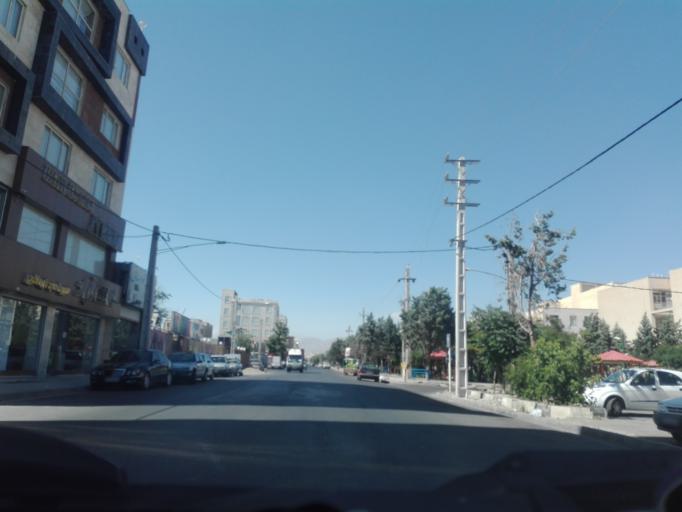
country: IR
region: Tehran
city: Shahre Jadide Andisheh
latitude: 35.7213
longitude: 50.9838
